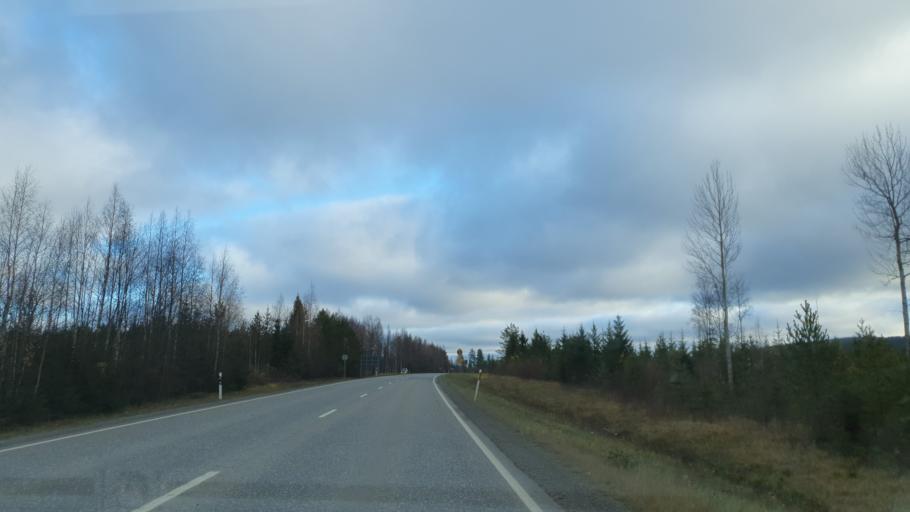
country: FI
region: Kainuu
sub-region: Kajaani
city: Vuokatti
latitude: 64.1178
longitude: 28.1786
